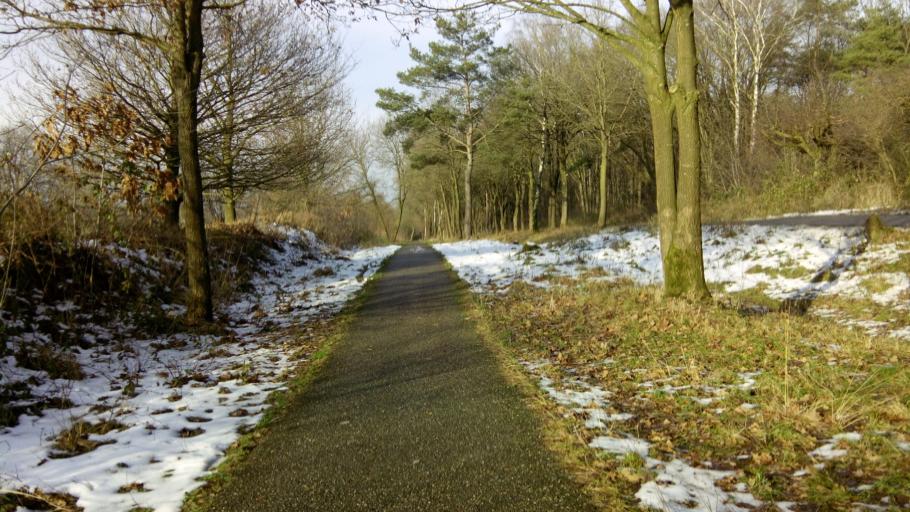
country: NL
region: Gelderland
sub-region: Gemeente Groesbeek
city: Groesbeek
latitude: 51.7803
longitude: 5.8907
